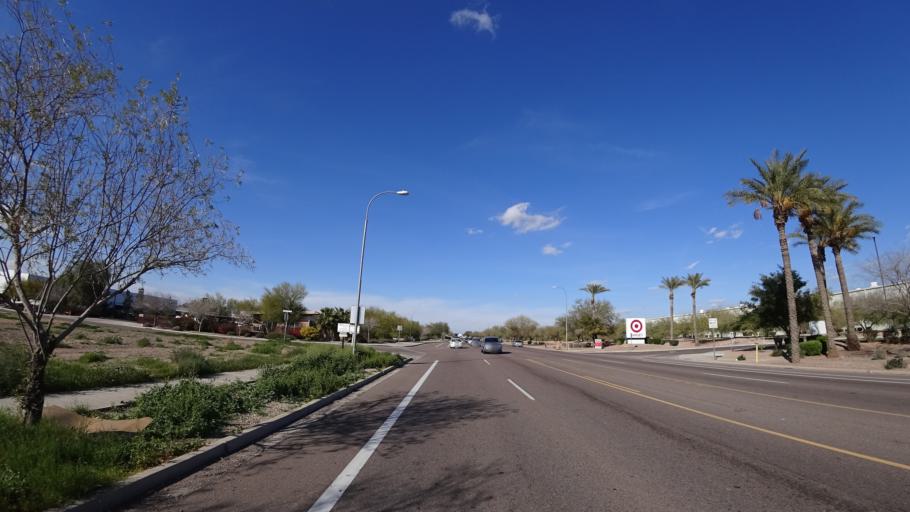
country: US
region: Arizona
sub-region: Maricopa County
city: Tolleson
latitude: 33.4465
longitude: -112.2212
